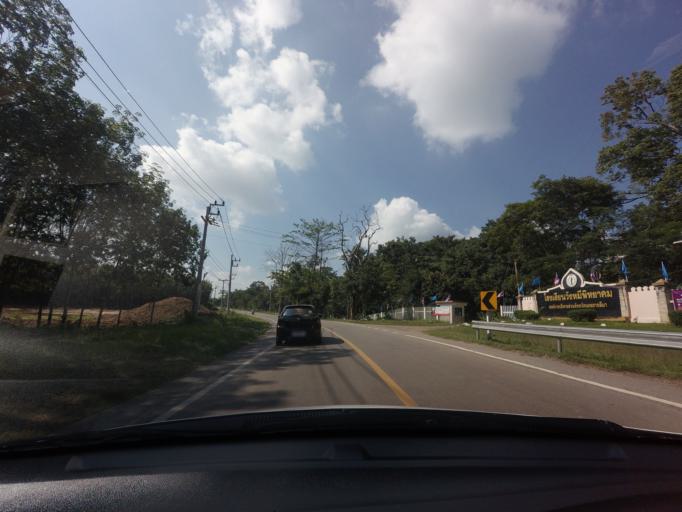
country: TH
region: Nakhon Ratchasima
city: Wang Nam Khiao
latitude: 14.4372
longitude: 101.6791
